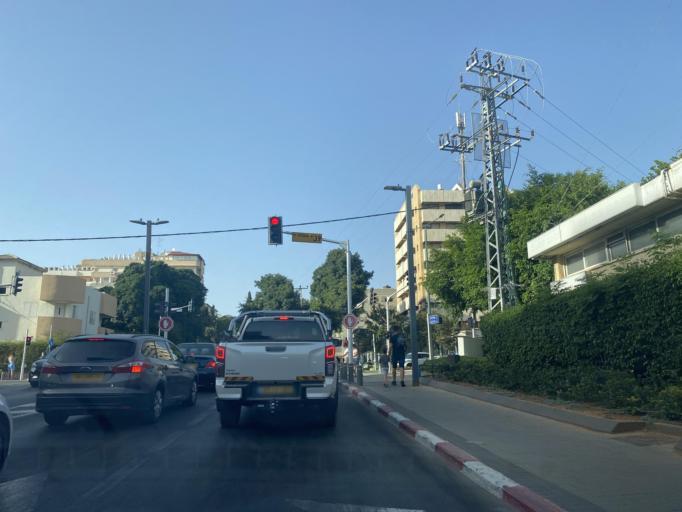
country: IL
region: Tel Aviv
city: Ramat HaSharon
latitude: 32.1668
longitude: 34.8487
